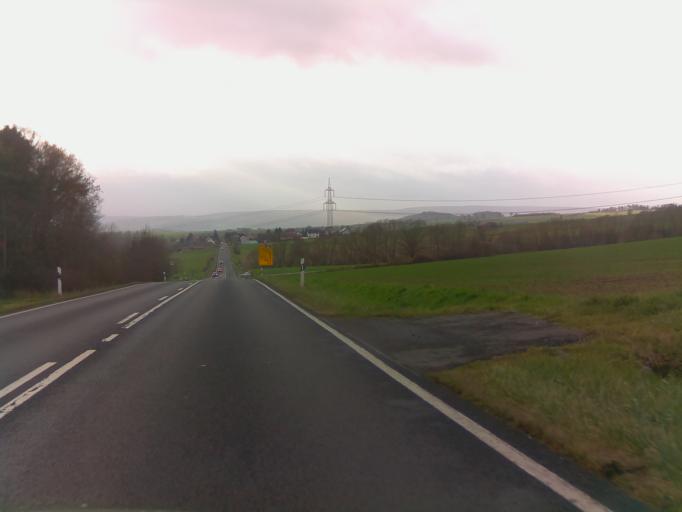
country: DE
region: Hesse
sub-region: Regierungsbezirk Kassel
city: Rasdorf
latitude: 50.7046
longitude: 9.8357
